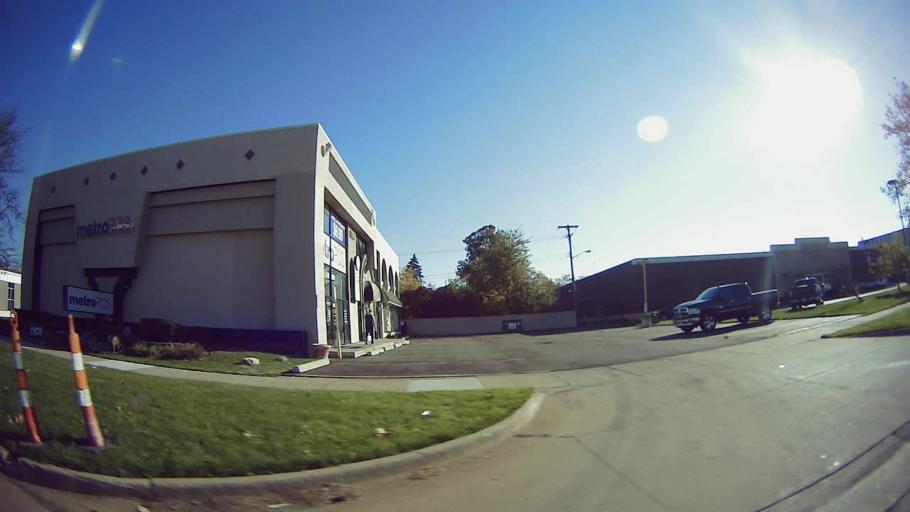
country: US
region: Michigan
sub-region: Oakland County
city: Oak Park
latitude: 42.4548
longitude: -83.2008
